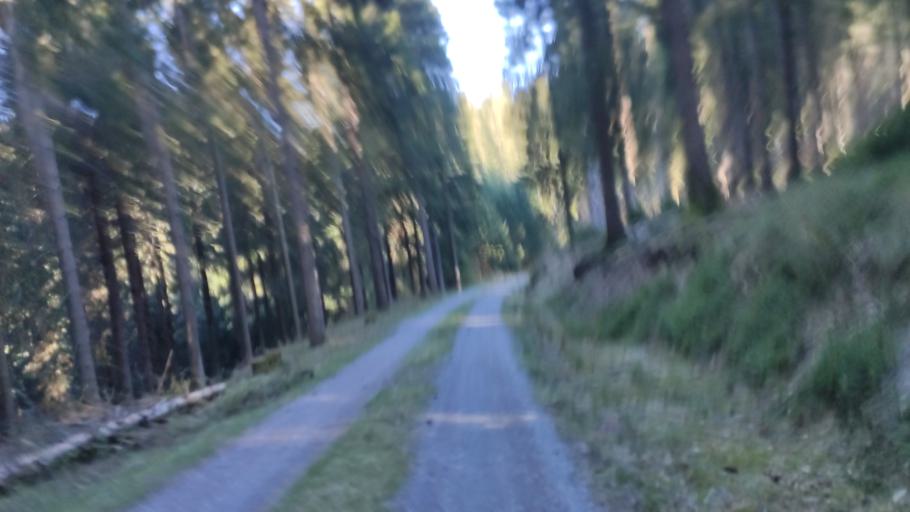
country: DE
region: Bavaria
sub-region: Upper Franconia
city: Reichenbach
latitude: 50.4442
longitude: 11.4365
